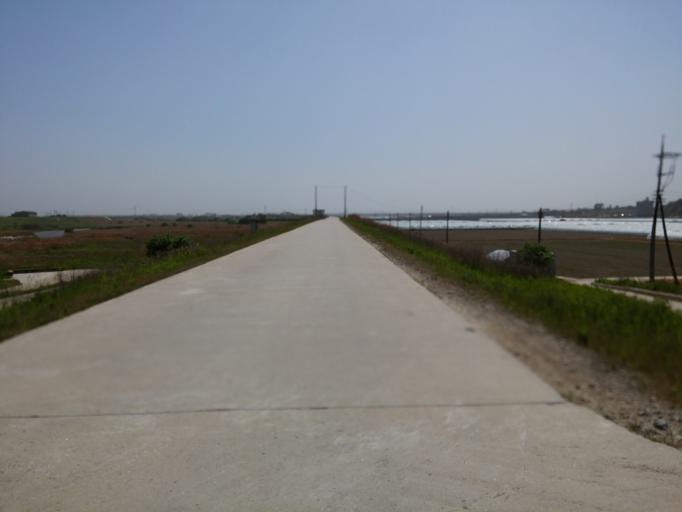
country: KR
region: Chungcheongnam-do
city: Nonsan
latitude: 36.2065
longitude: 127.0731
